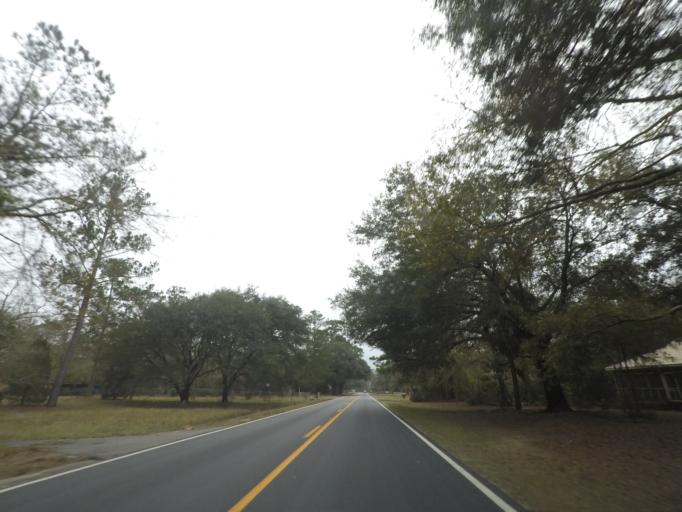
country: US
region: South Carolina
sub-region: Charleston County
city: Ravenel
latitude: 32.7290
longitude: -80.3526
